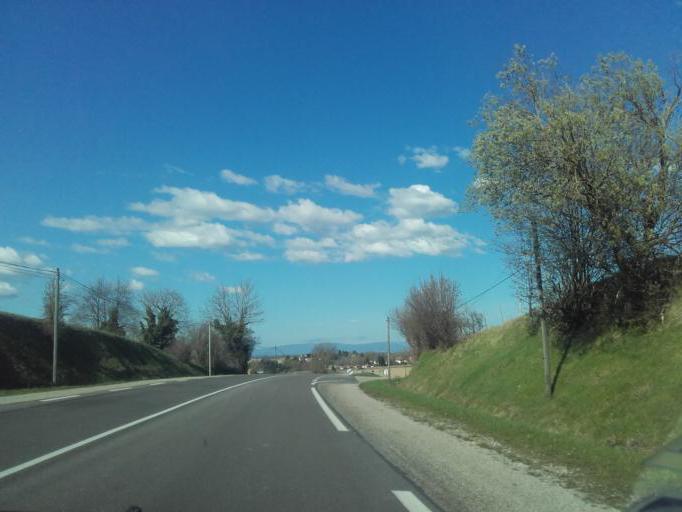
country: FR
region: Rhone-Alpes
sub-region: Departement de l'Isere
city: Champier
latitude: 45.4916
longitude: 5.2962
